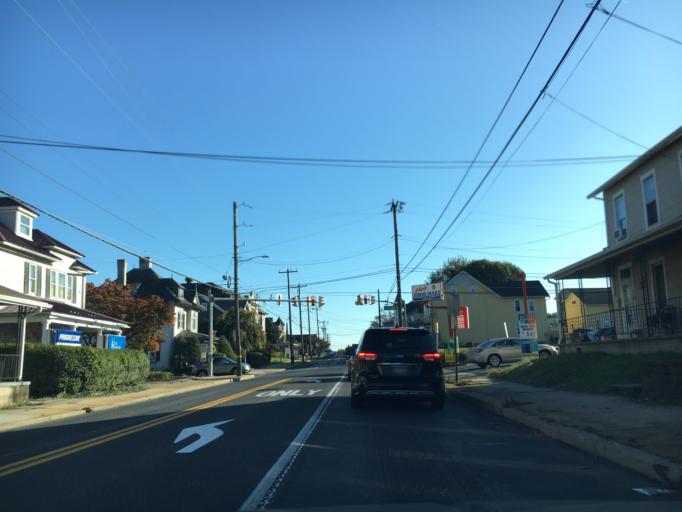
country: US
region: Pennsylvania
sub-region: Lehigh County
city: Fullerton
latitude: 40.6367
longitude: -75.4709
